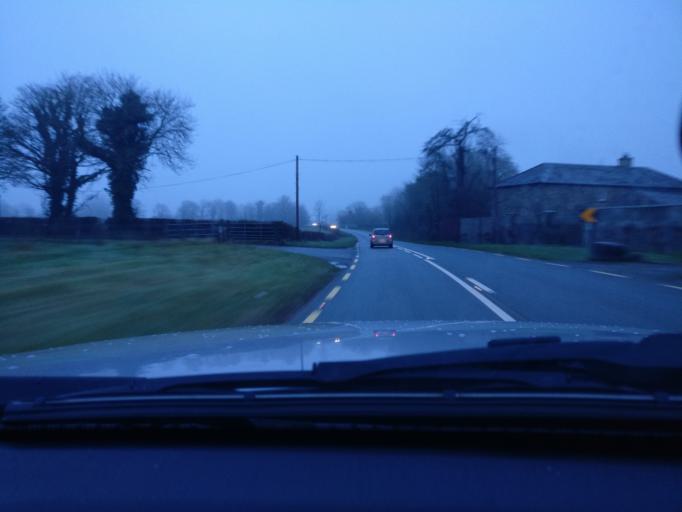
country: IE
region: Leinster
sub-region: An Mhi
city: Athboy
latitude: 53.6419
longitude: -6.8802
